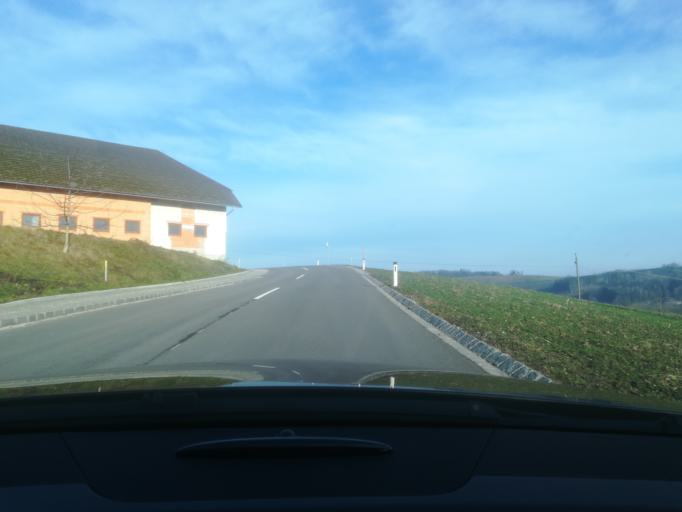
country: AT
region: Upper Austria
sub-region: Wels-Land
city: Buchkirchen
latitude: 48.2489
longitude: 14.0396
